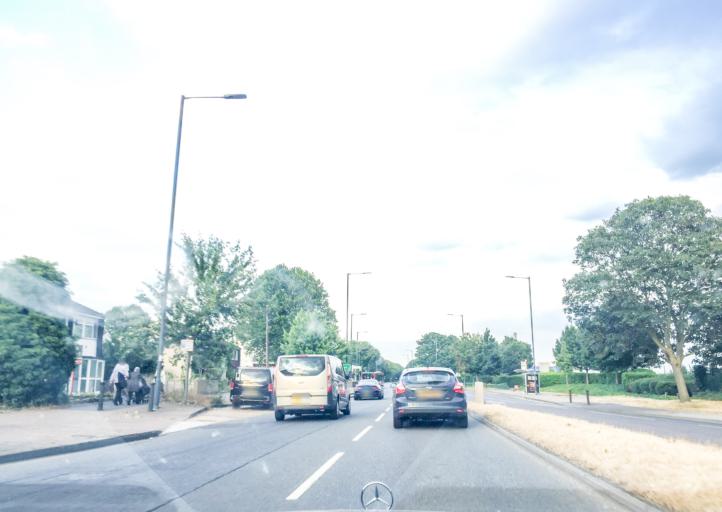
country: GB
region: England
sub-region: Greater London
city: West Drayton
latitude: 51.4818
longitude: -0.4764
